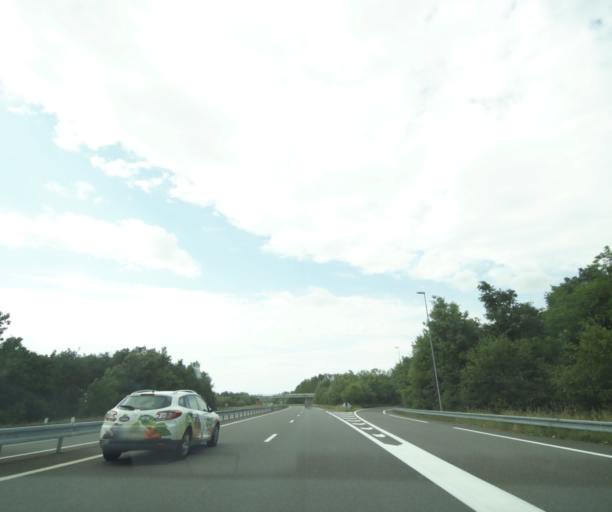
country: FR
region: Pays de la Loire
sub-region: Departement de Maine-et-Loire
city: Beaufort-en-Vallee
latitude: 47.4704
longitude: -0.1896
